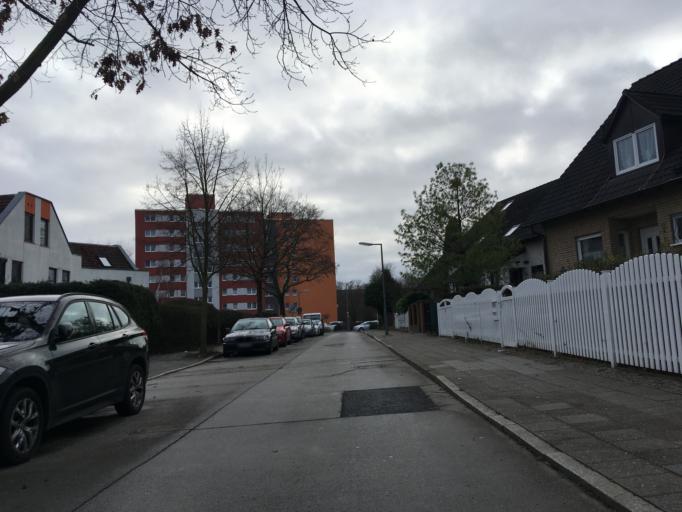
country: DE
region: Berlin
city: Markisches Viertel
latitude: 52.5931
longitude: 13.3556
